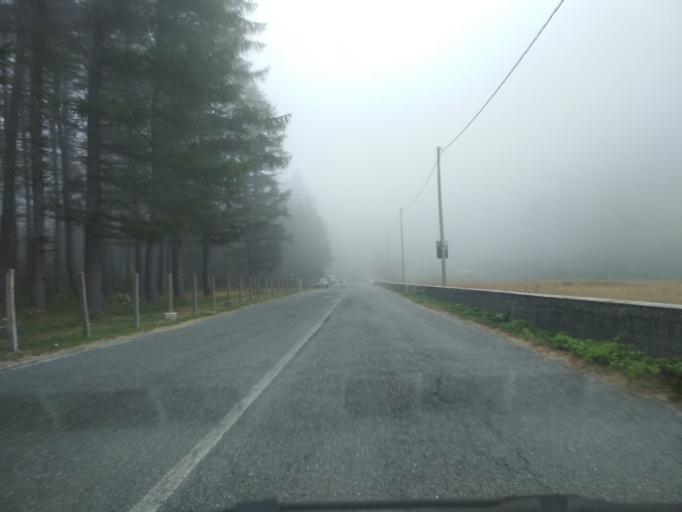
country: IT
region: Piedmont
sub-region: Provincia di Torino
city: Balme
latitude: 45.3026
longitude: 7.1896
